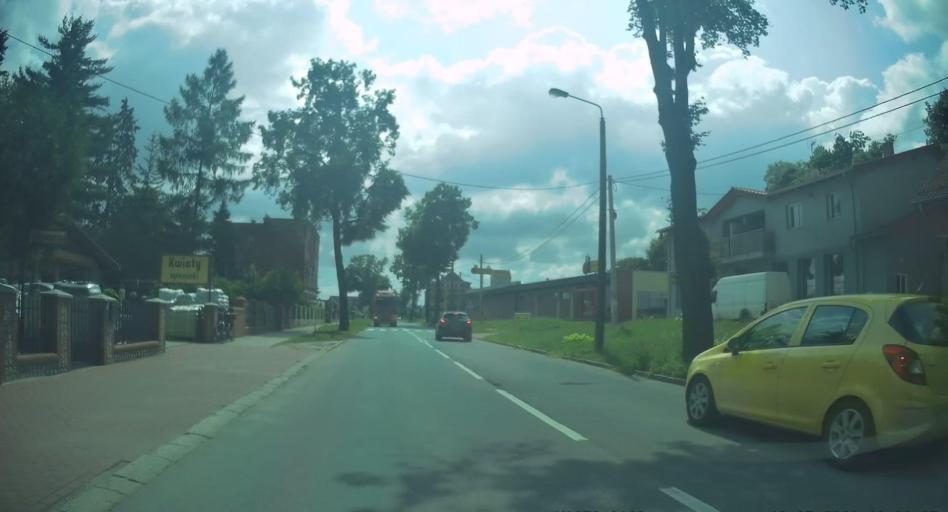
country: PL
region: Opole Voivodeship
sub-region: Powiat prudnicki
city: Glogowek
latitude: 50.3521
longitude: 17.8698
